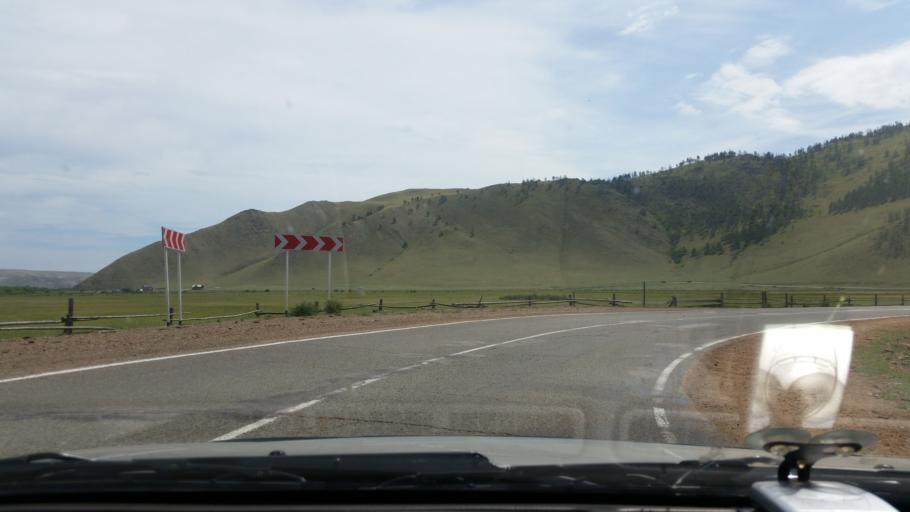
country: RU
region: Irkutsk
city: Yelantsy
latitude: 52.8053
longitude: 106.4702
